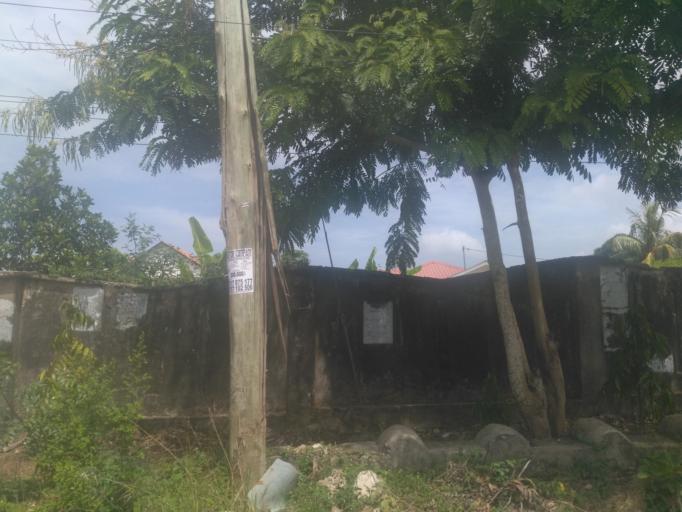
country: TZ
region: Zanzibar Urban/West
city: Zanzibar
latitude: -6.2298
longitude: 39.2119
